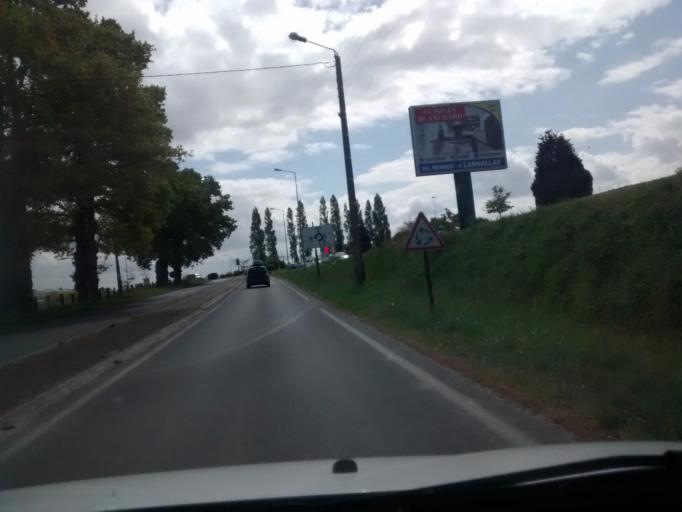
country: FR
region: Brittany
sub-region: Departement des Cotes-d'Armor
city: Lanvallay
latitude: 48.4727
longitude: -2.0435
